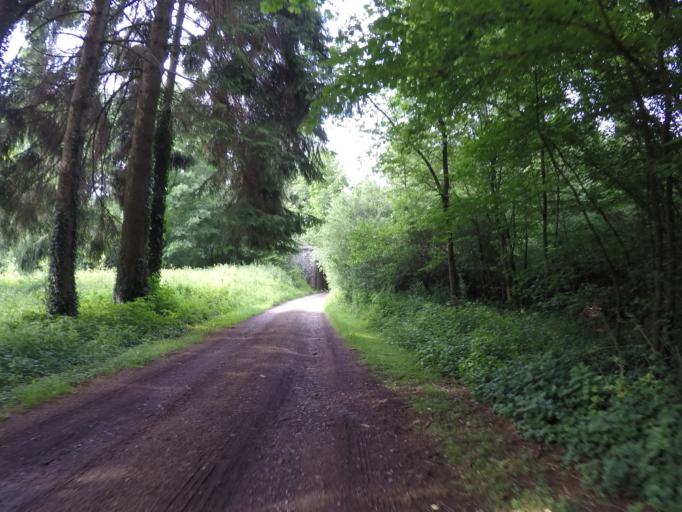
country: BE
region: Wallonia
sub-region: Province de Namur
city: Assesse
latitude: 50.3164
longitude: 5.0244
